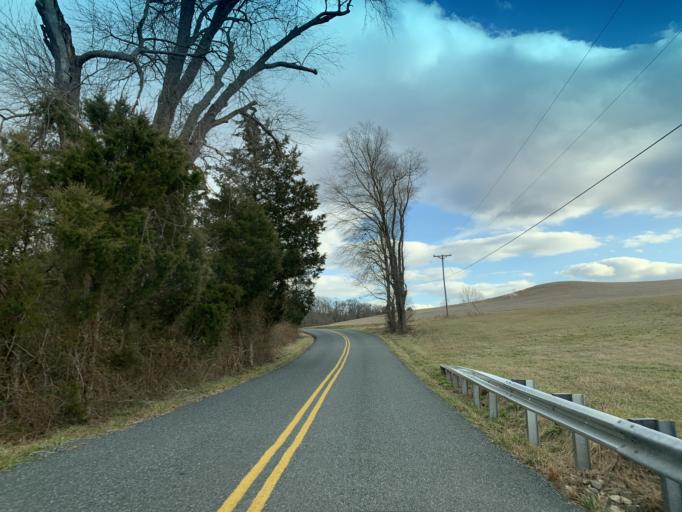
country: US
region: Maryland
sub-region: Harford County
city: South Bel Air
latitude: 39.5775
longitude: -76.2974
